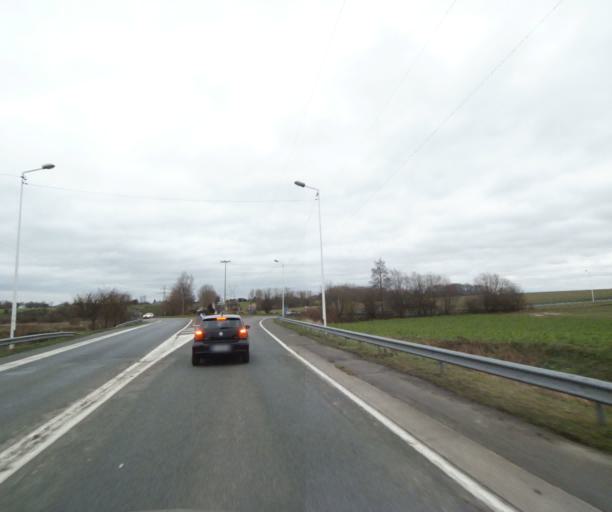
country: FR
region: Nord-Pas-de-Calais
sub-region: Departement du Nord
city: Marly
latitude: 50.3540
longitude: 3.5594
